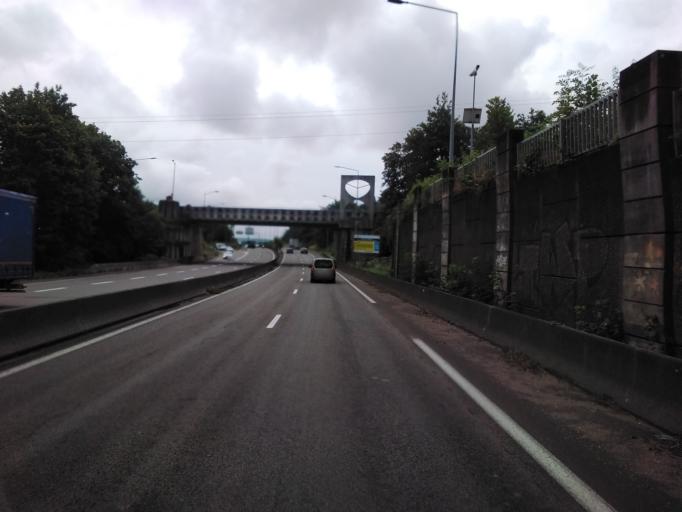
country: FR
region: Franche-Comte
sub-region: Departement du Doubs
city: Miserey-Salines
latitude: 47.2724
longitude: 5.9971
